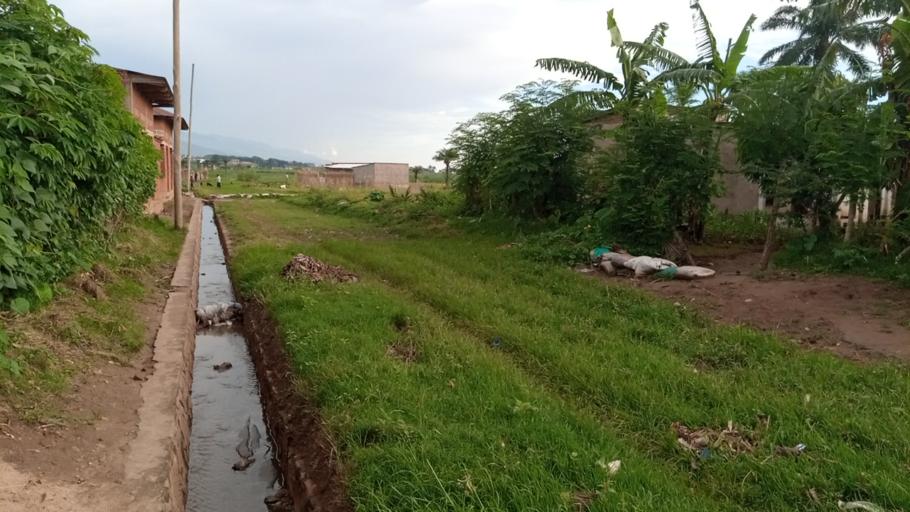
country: BI
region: Bujumbura Mairie
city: Bujumbura
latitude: -3.4267
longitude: 29.3468
